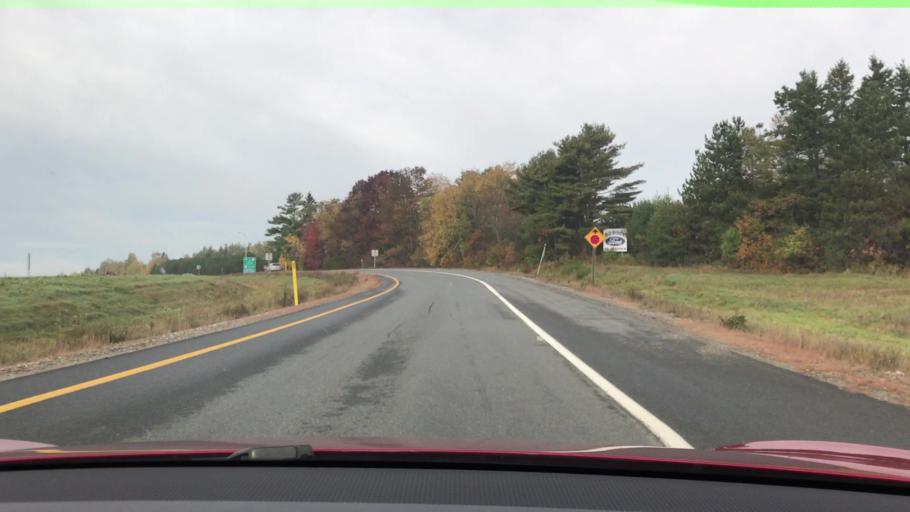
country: US
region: Maine
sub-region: Washington County
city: Calais
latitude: 45.2117
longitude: -67.2704
